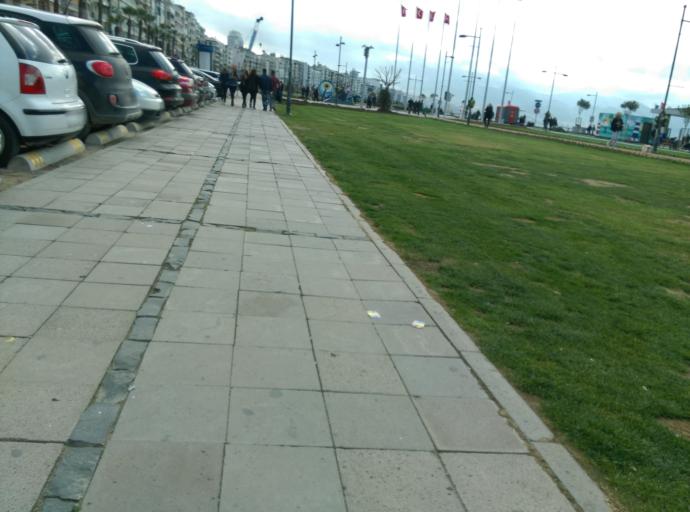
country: TR
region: Izmir
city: Izmir
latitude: 38.4394
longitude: 27.1419
